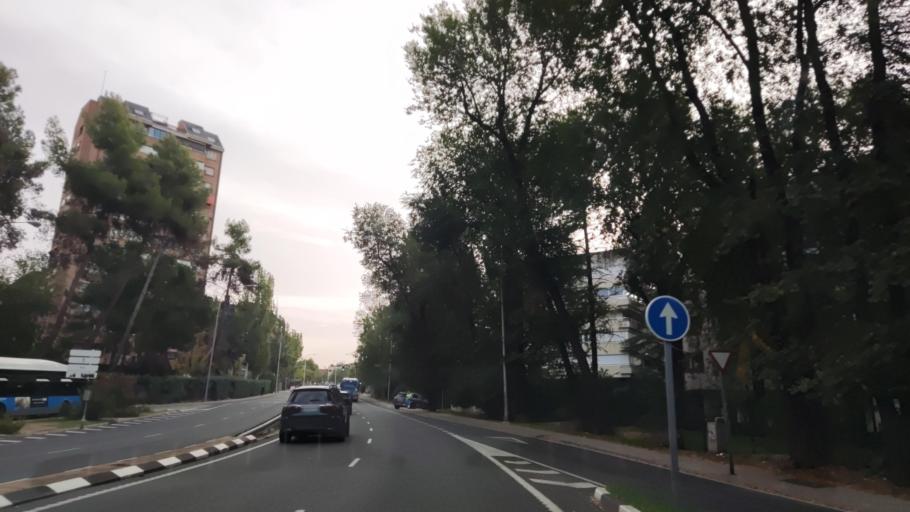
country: ES
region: Madrid
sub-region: Provincia de Madrid
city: Fuencarral-El Pardo
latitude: 40.4768
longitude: -3.7406
